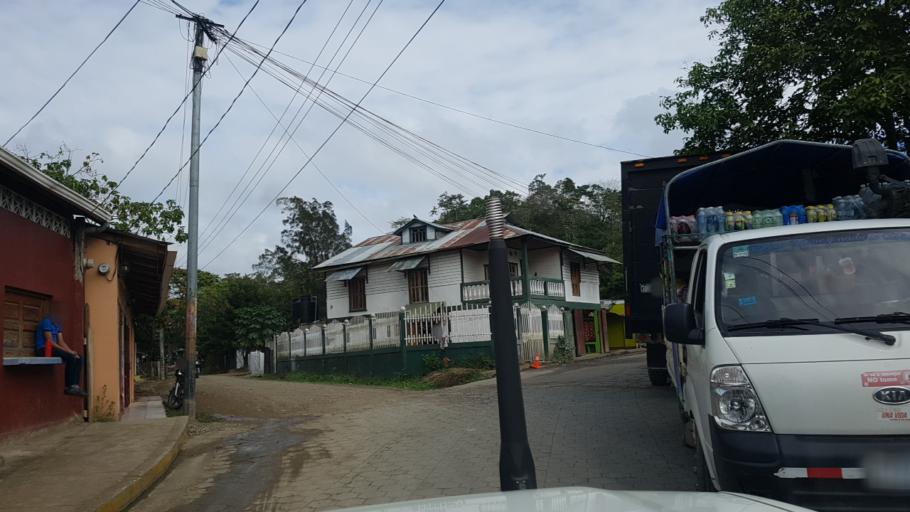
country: NI
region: Atlantico Norte (RAAN)
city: Siuna
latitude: 13.7402
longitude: -84.7817
